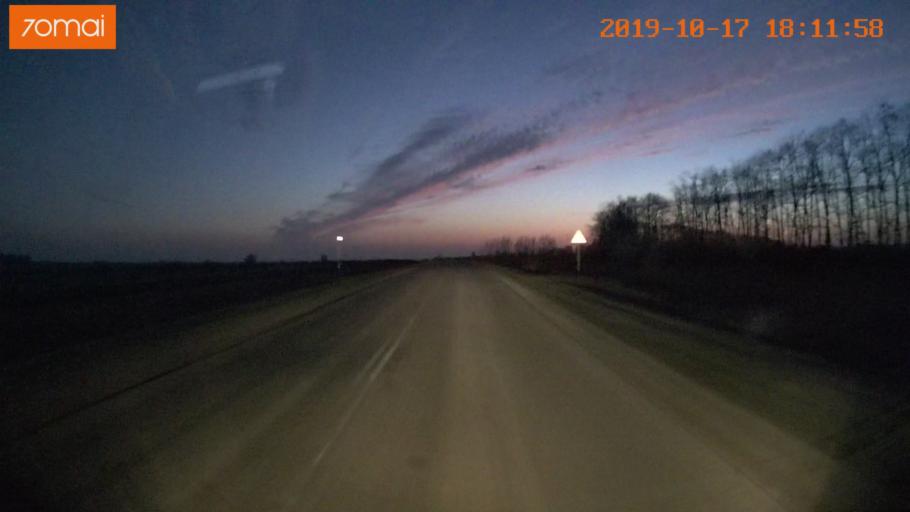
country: RU
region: Tula
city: Kurkino
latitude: 53.4125
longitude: 38.6198
